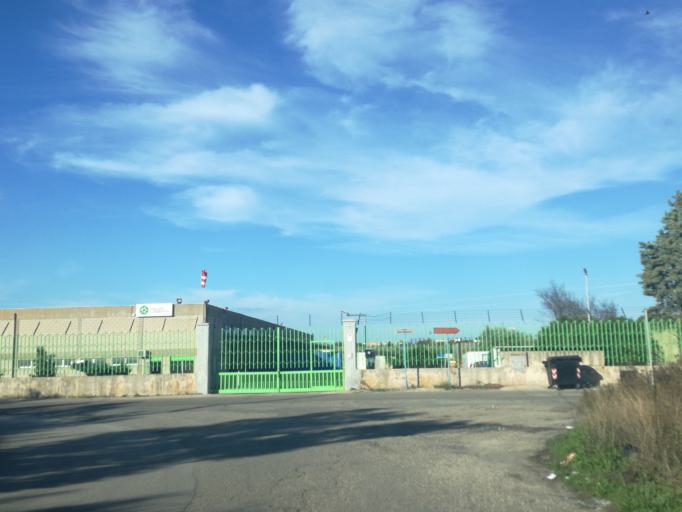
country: IT
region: Apulia
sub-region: Provincia di Bari
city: San Paolo
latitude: 41.1261
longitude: 16.8172
